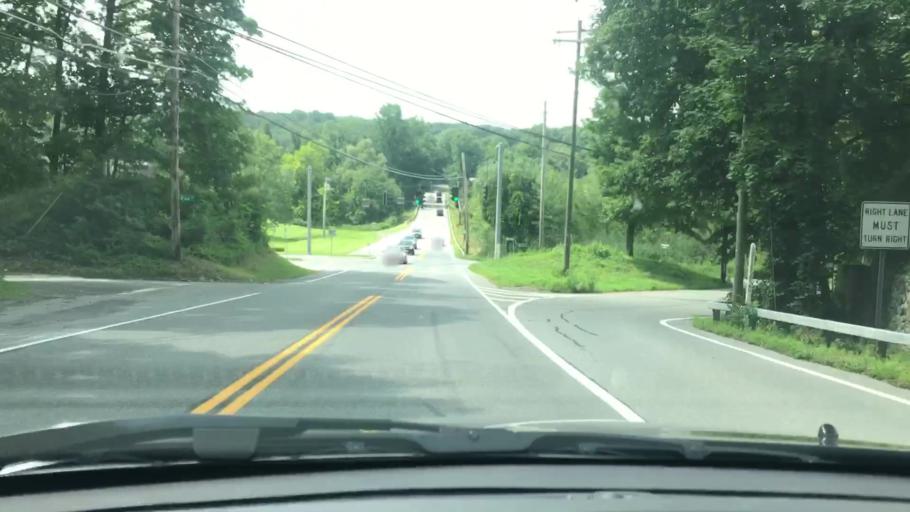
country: US
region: New York
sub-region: Westchester County
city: Bedford
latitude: 41.1946
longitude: -73.6738
